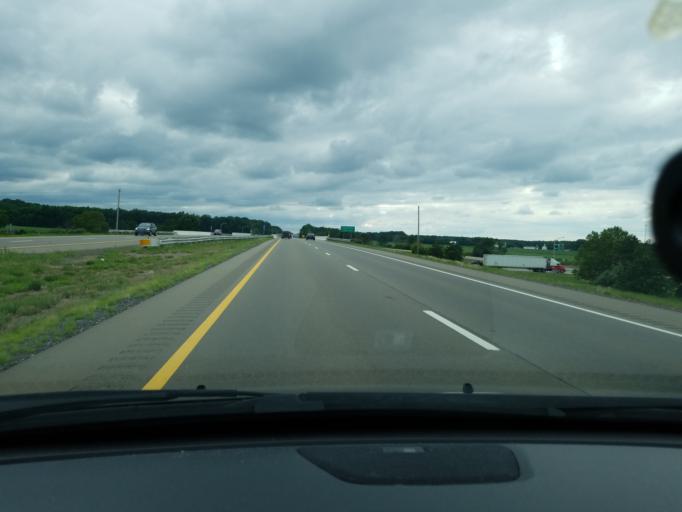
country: US
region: Ohio
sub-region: Lorain County
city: Vermilion-on-the-Lake
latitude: 41.4038
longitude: -82.2811
